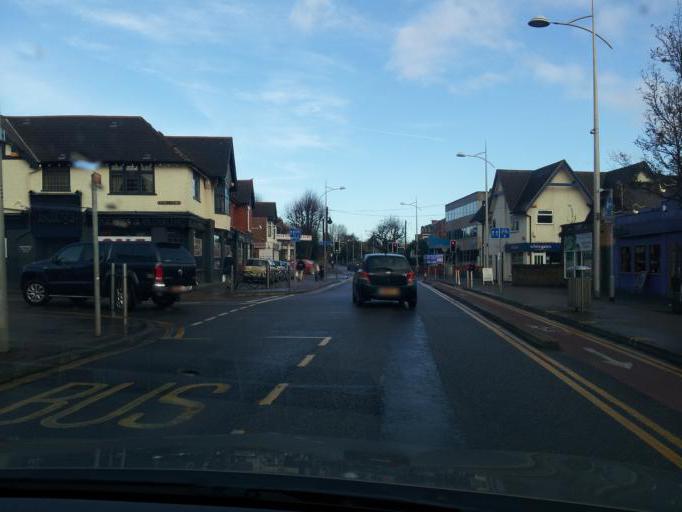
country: GB
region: England
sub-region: Nottinghamshire
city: Gotham
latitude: 52.9294
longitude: -1.2109
